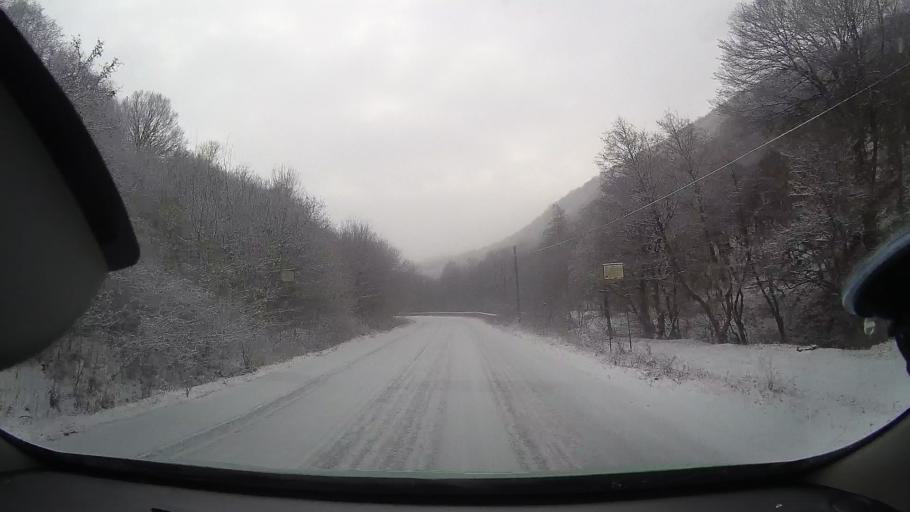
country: RO
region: Alba
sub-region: Comuna Rimetea
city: Rimetea
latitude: 46.4931
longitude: 23.5796
